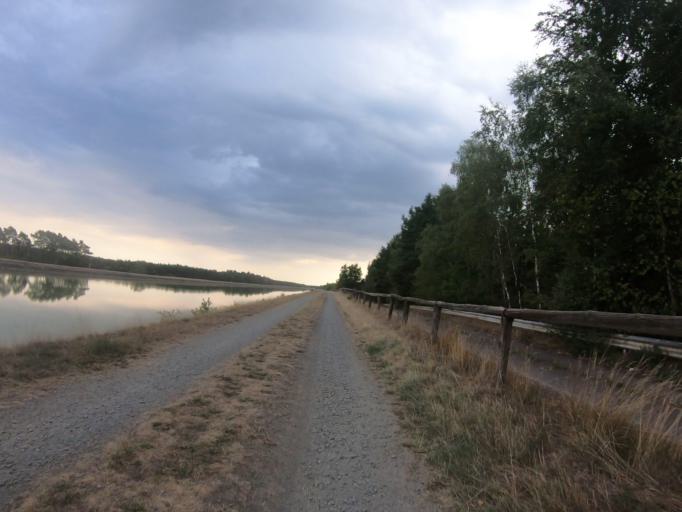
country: DE
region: Lower Saxony
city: Sassenburg
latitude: 52.5546
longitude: 10.6604
